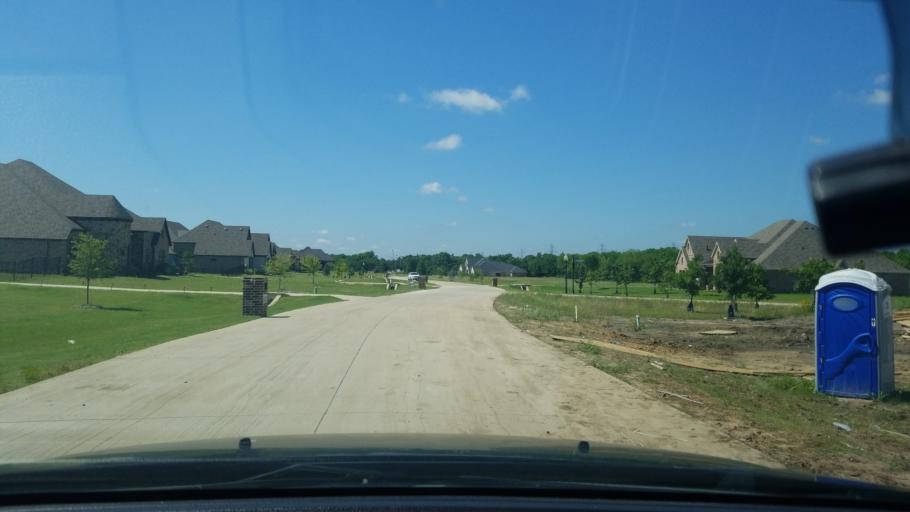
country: US
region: Texas
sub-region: Dallas County
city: Sunnyvale
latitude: 32.8018
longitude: -96.5705
